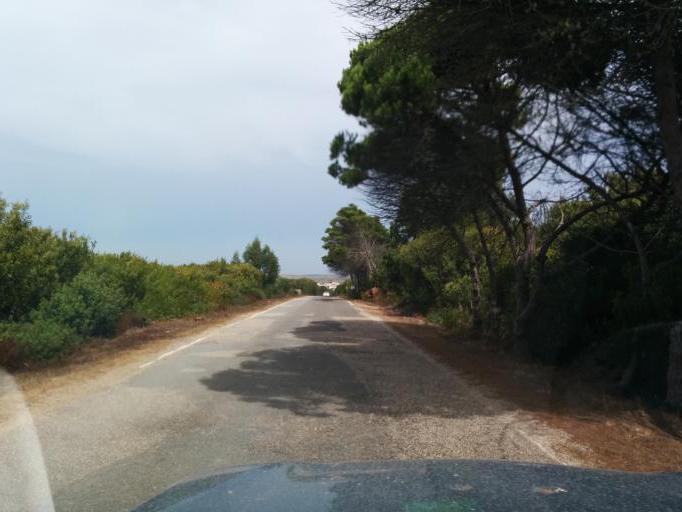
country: PT
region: Beja
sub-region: Odemira
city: Vila Nova de Milfontes
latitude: 37.7145
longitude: -8.7797
